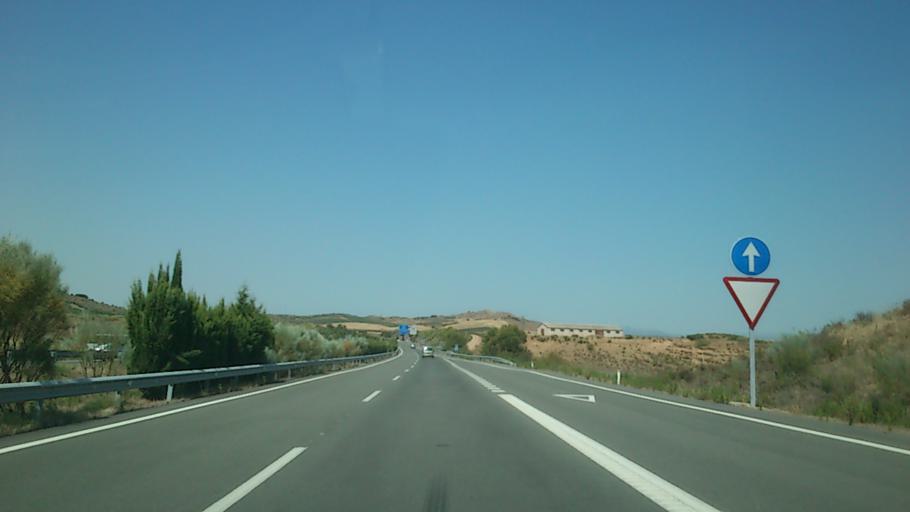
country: ES
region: Navarre
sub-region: Provincia de Navarra
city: Sartaguda
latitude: 42.3642
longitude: -2.0700
